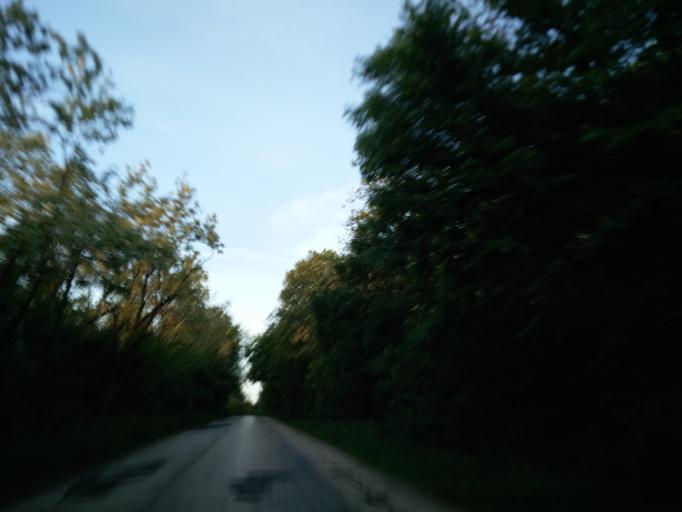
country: HU
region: Fejer
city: Etyek
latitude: 47.4396
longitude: 18.7005
